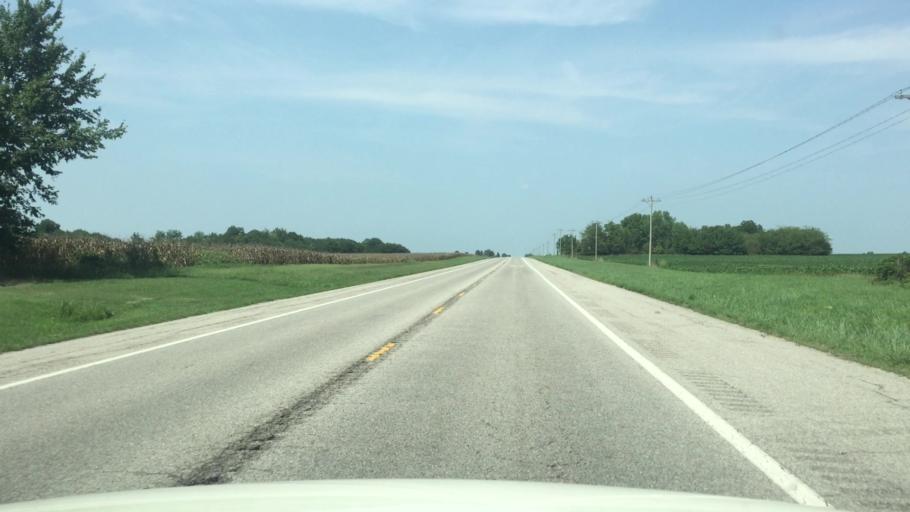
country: US
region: Kansas
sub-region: Crawford County
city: Pittsburg
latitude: 37.2583
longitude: -94.7052
